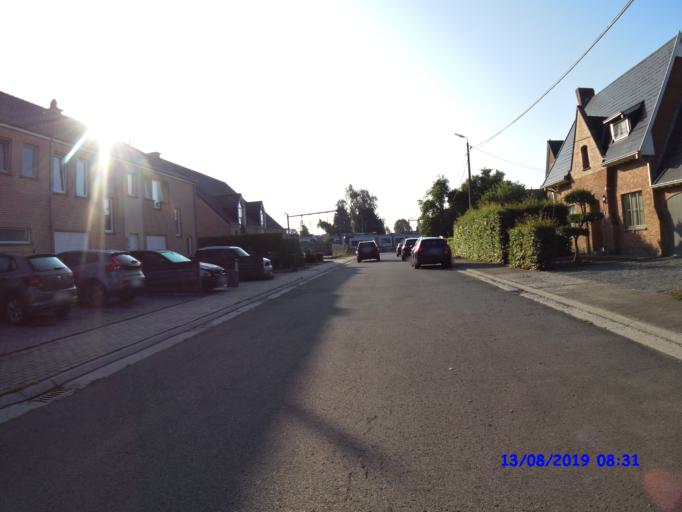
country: BE
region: Flanders
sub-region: Provincie Oost-Vlaanderen
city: Dendermonde
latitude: 51.0207
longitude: 4.1180
